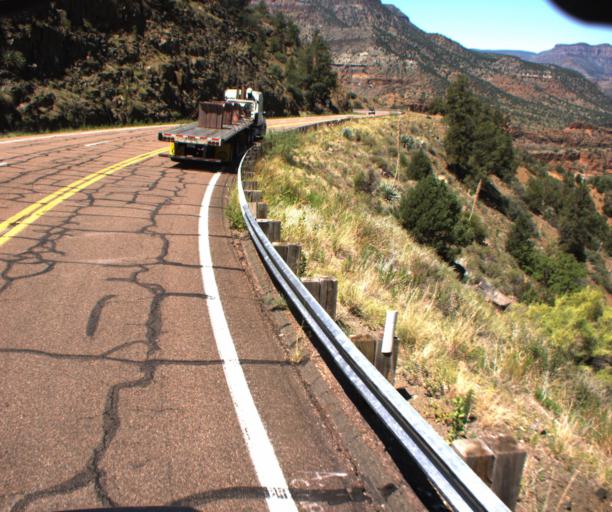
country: US
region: Arizona
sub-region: Navajo County
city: Cibecue
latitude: 33.7936
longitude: -110.5005
